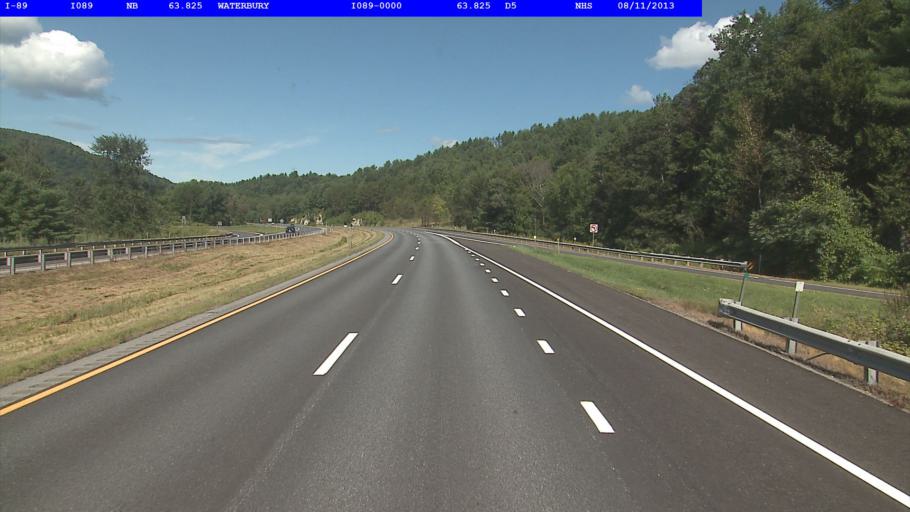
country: US
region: Vermont
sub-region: Washington County
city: Waterbury
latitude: 44.3438
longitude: -72.7531
